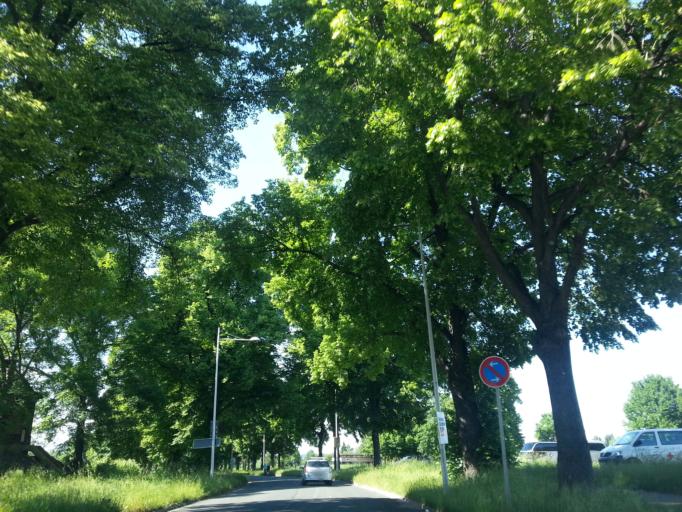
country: DE
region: Saxony
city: Dresden
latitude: 51.0622
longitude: 13.7286
